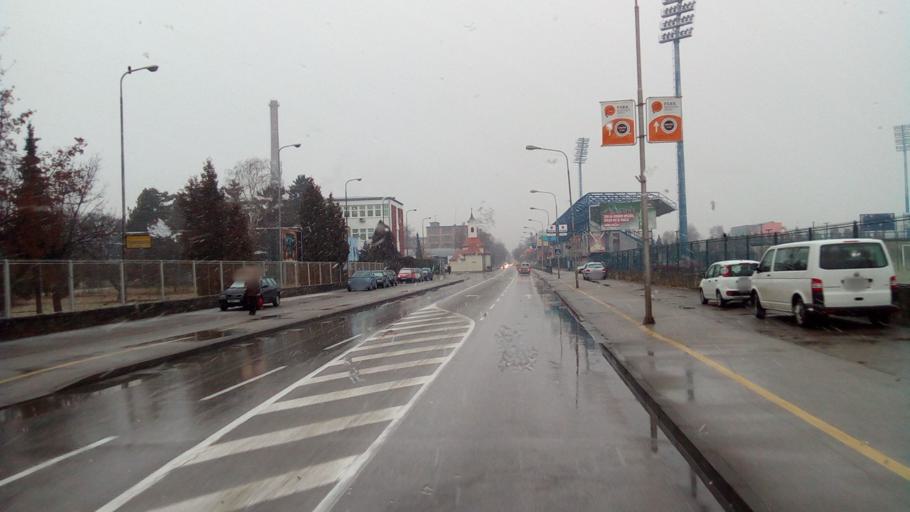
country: HR
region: Varazdinska
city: Varazdin
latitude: 46.2914
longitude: 16.3444
